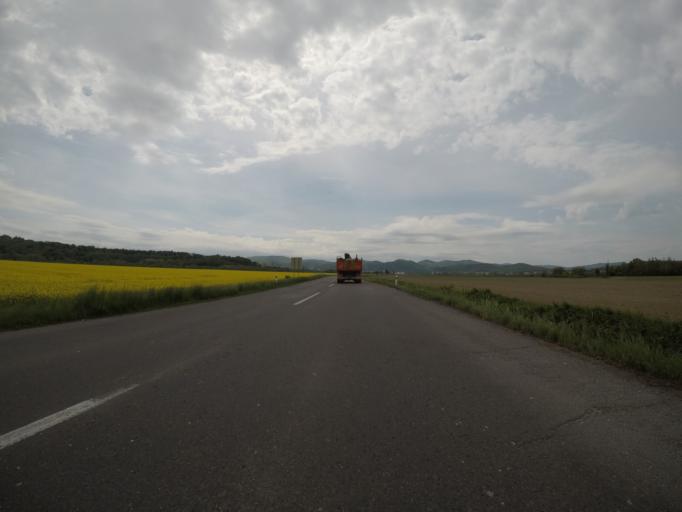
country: SK
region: Banskobystricky
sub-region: Okres Banska Bystrica
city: Zvolen
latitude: 48.6087
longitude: 19.1266
